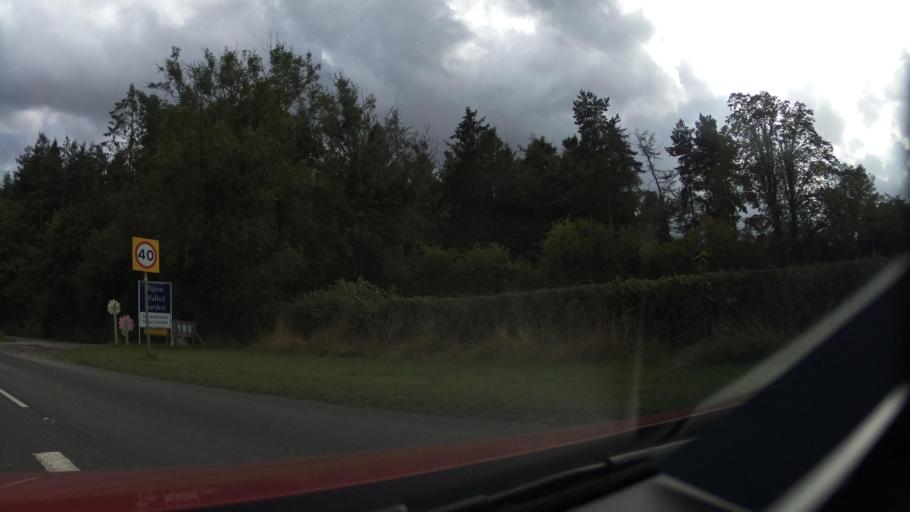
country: GB
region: England
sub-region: North Yorkshire
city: Ripon
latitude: 54.1553
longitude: -1.5395
